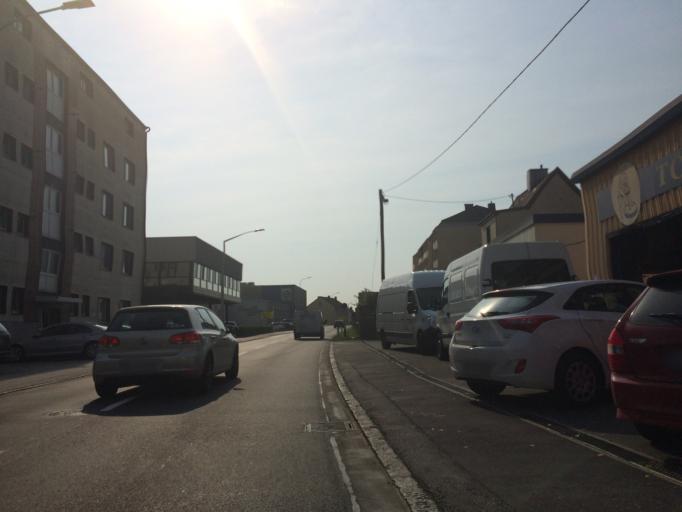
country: AT
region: Upper Austria
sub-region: Politischer Bezirk Linz-Land
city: Leonding
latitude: 48.2741
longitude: 14.2694
